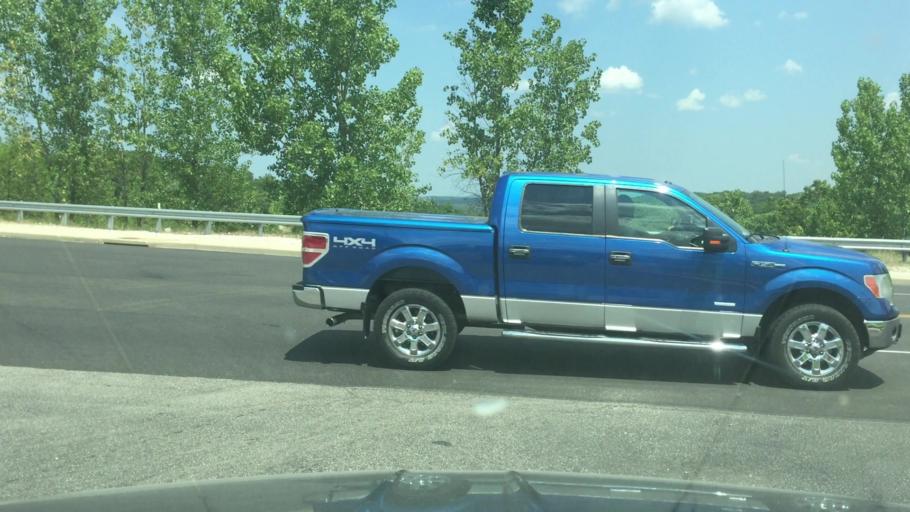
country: US
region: Missouri
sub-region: Miller County
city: Lake Ozark
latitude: 38.1618
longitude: -92.6059
